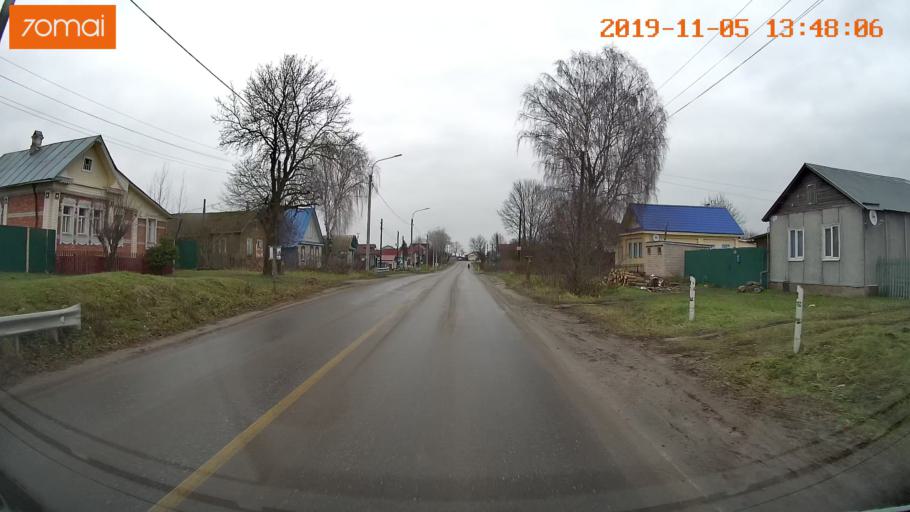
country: RU
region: Ivanovo
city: Shuya
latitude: 57.0016
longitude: 41.4046
